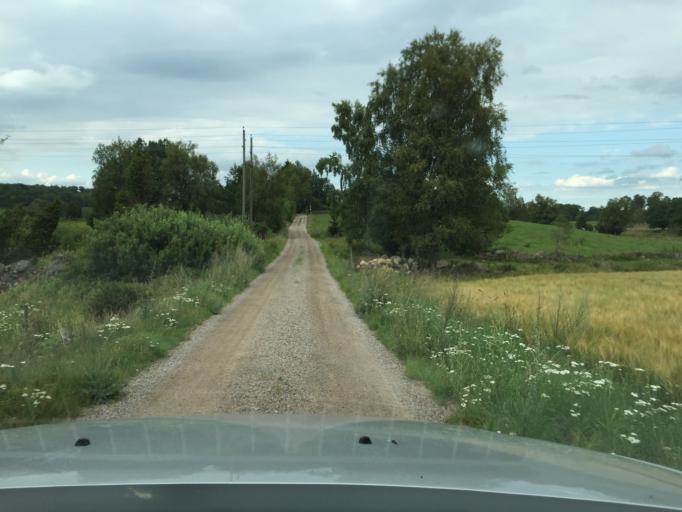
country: SE
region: Skane
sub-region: Hassleholms Kommun
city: Sosdala
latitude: 56.0501
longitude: 13.6897
